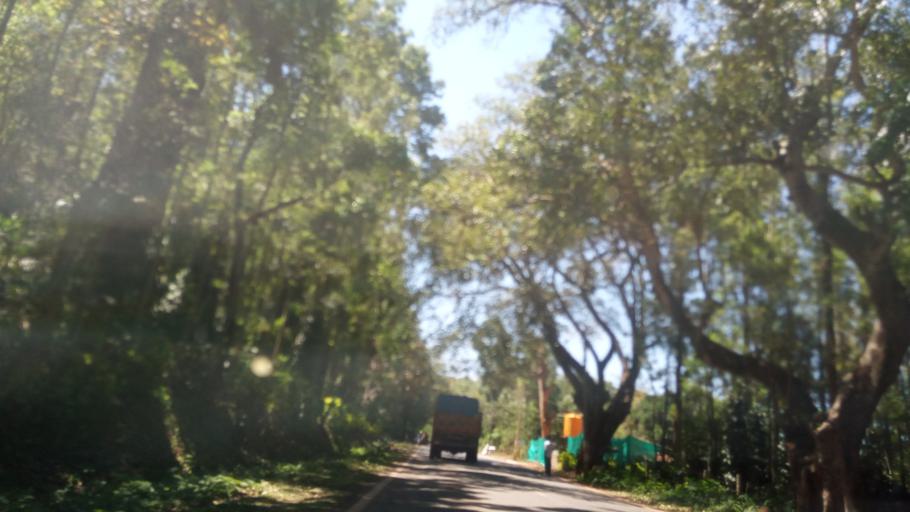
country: IN
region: Karnataka
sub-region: Chikmagalur
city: Chikmagalur
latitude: 13.3791
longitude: 75.7486
